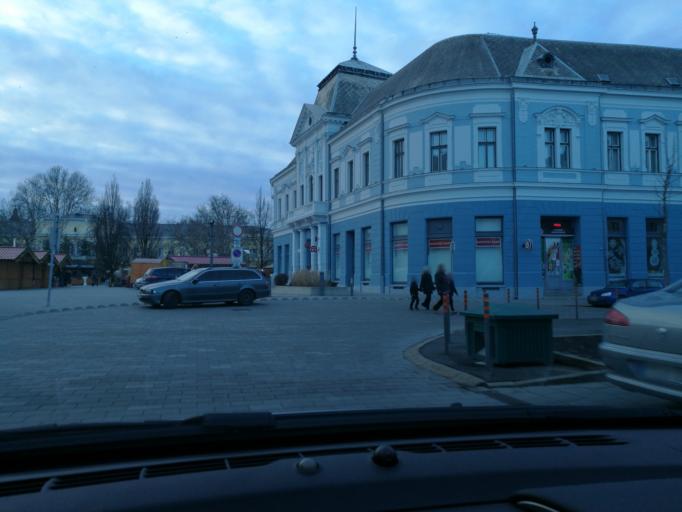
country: HU
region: Szabolcs-Szatmar-Bereg
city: Nyiregyhaza
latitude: 47.9556
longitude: 21.7182
